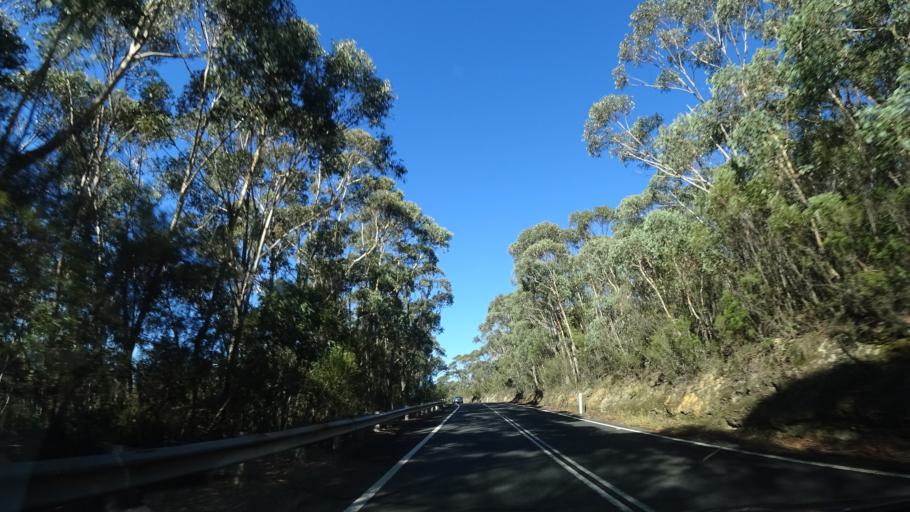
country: AU
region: New South Wales
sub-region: Blue Mountains Municipality
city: Blackheath
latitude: -33.5653
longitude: 150.3650
